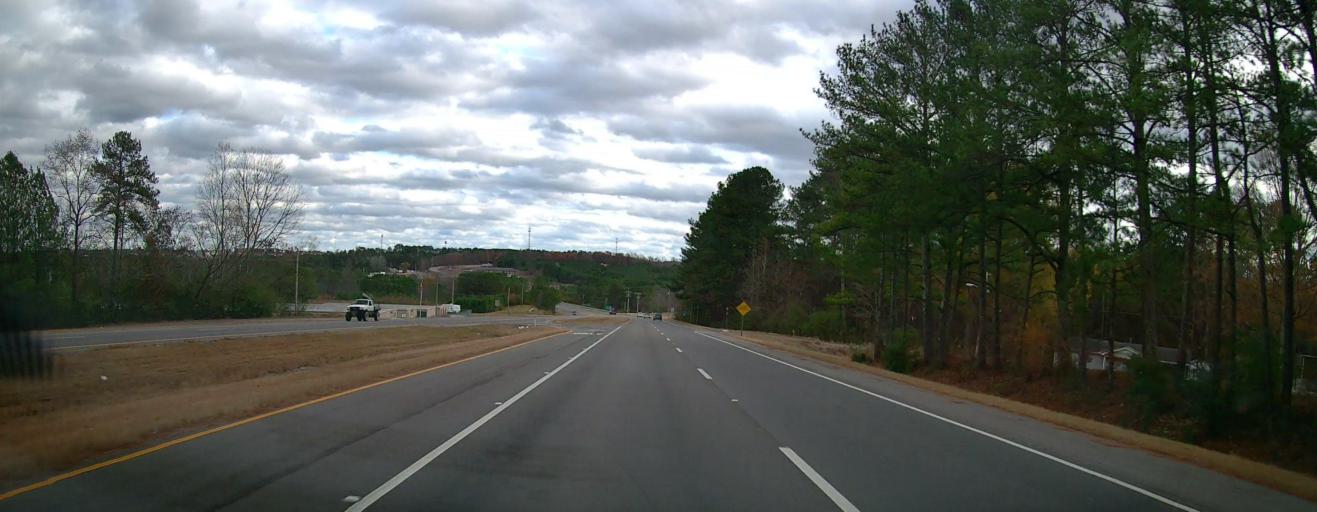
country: US
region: Alabama
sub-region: Cullman County
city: Cullman
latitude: 34.2130
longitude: -86.8901
